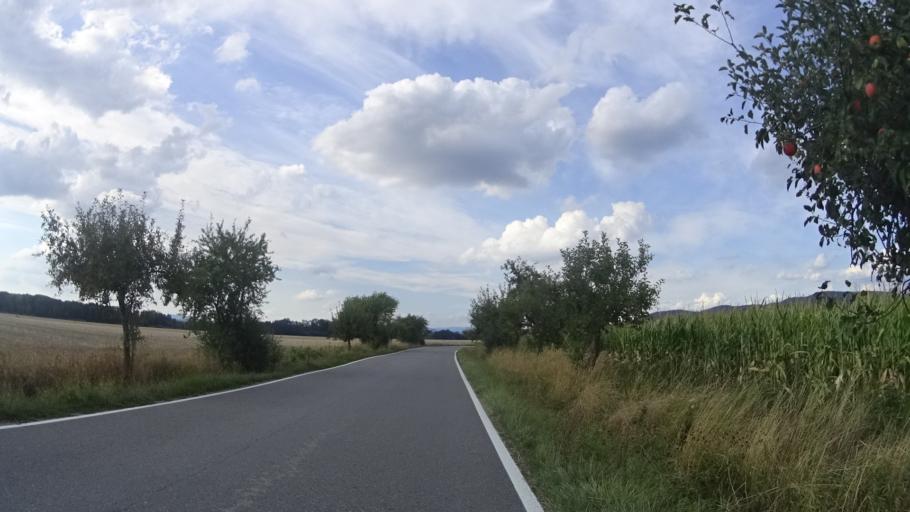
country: CZ
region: Olomoucky
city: Dubicko
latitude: 49.8290
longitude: 16.9356
